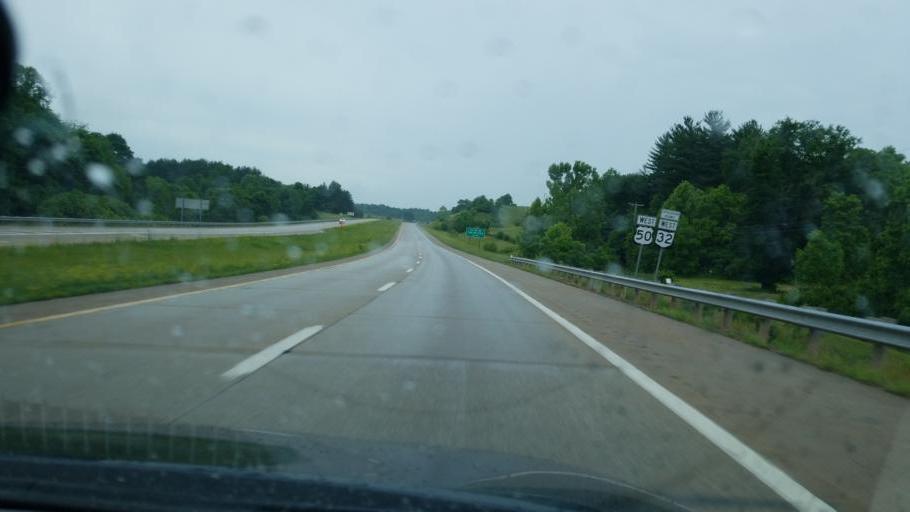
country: US
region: Ohio
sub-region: Athens County
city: Athens
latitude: 39.2495
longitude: -81.8966
